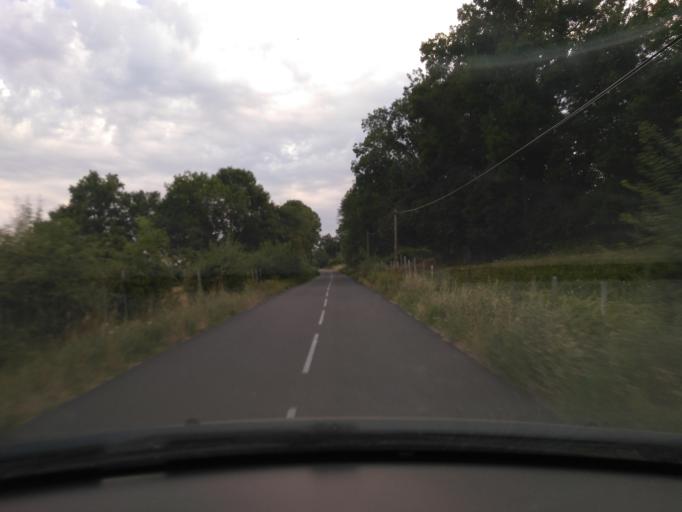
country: FR
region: Rhone-Alpes
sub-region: Departement de l'Isere
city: Beaurepaire
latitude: 45.3993
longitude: 5.1234
